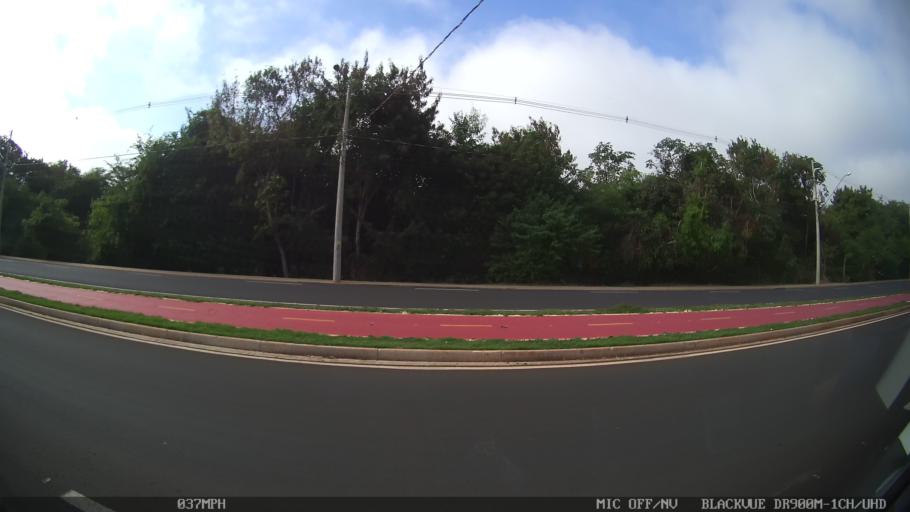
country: BR
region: Sao Paulo
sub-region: Sao Jose Do Rio Preto
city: Sao Jose do Rio Preto
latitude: -20.8126
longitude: -49.4338
